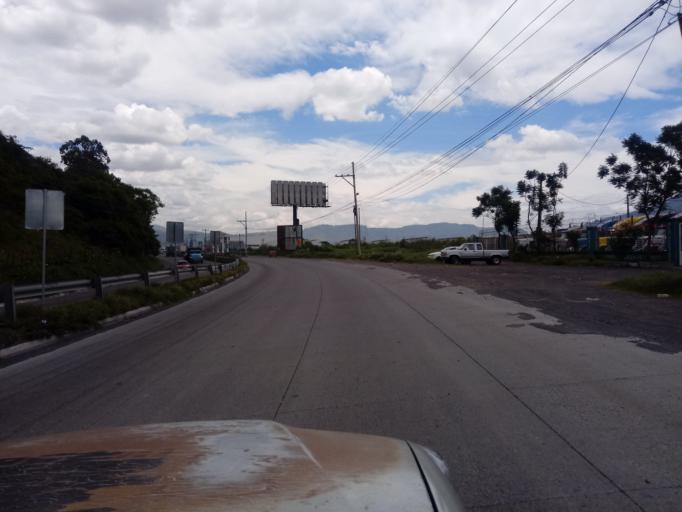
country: GT
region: Escuintla
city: San Vicente Pacaya
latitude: 14.4486
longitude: -90.6443
